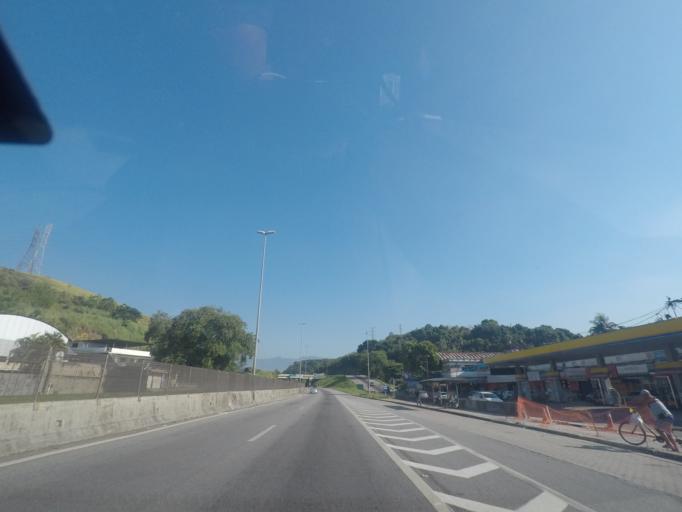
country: BR
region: Rio de Janeiro
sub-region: Duque De Caxias
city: Duque de Caxias
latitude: -22.6413
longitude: -43.2837
